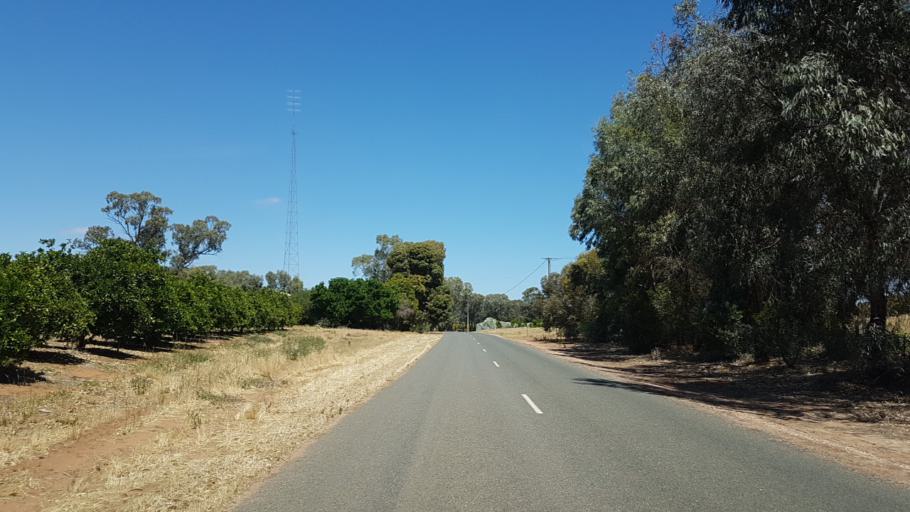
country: AU
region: South Australia
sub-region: Loxton Waikerie
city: Waikerie
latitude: -34.1646
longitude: 140.0304
